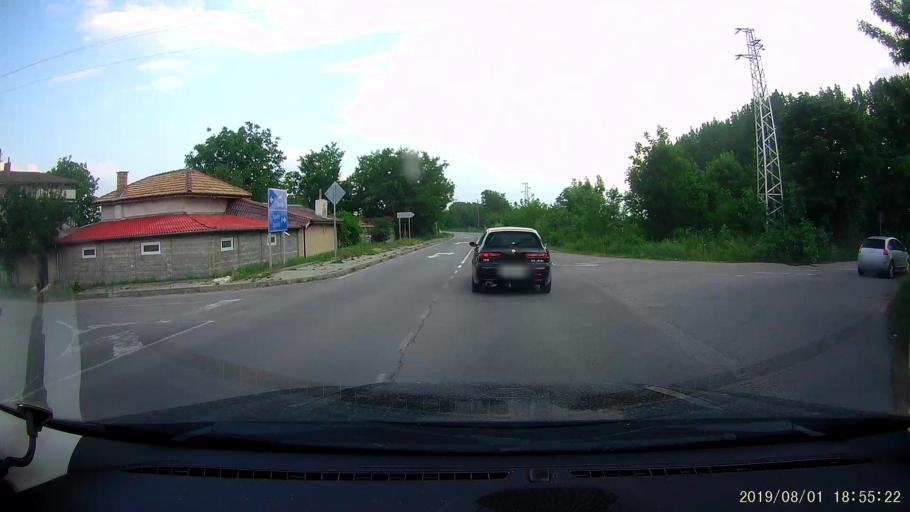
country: BG
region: Shumen
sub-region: Obshtina Smyadovo
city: Smyadovo
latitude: 43.1818
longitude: 27.0056
